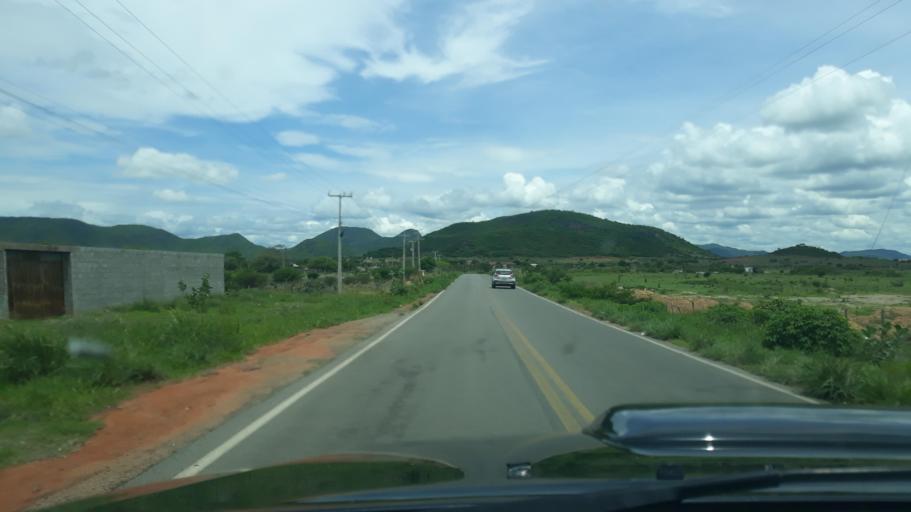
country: BR
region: Bahia
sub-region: Guanambi
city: Guanambi
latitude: -14.2517
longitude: -42.7458
